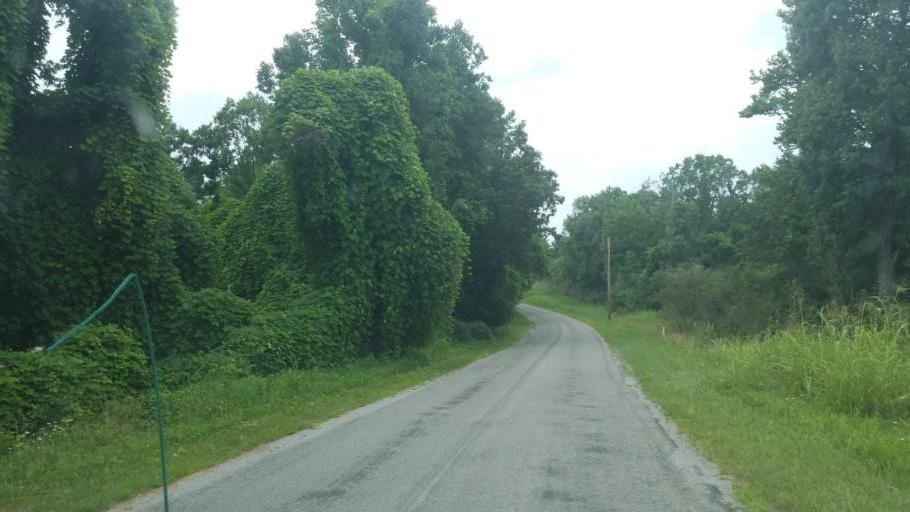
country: US
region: Illinois
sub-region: Jackson County
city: Murphysboro
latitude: 37.6850
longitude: -89.3849
